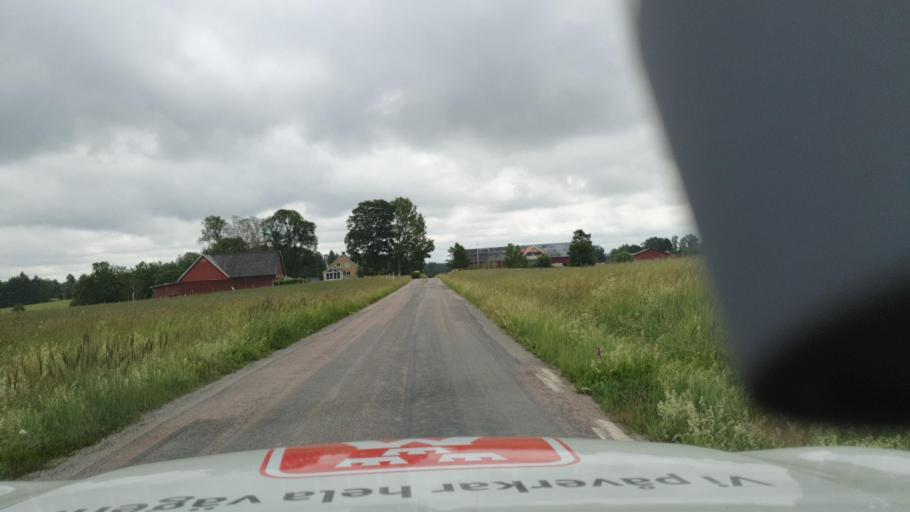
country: SE
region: Vaestra Goetaland
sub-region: Falkopings Kommun
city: Falkoeping
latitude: 57.9896
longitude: 13.4727
